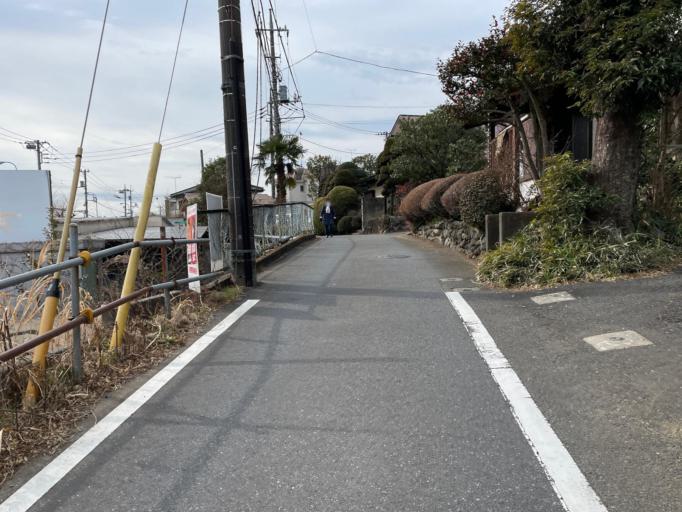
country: JP
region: Tokyo
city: Hino
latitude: 35.6516
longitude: 139.4372
